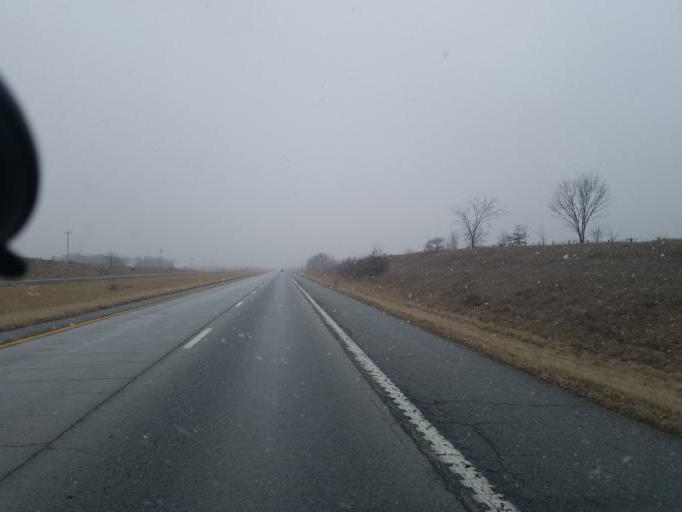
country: US
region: Missouri
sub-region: Macon County
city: La Plata
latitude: 39.9680
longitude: -92.4765
